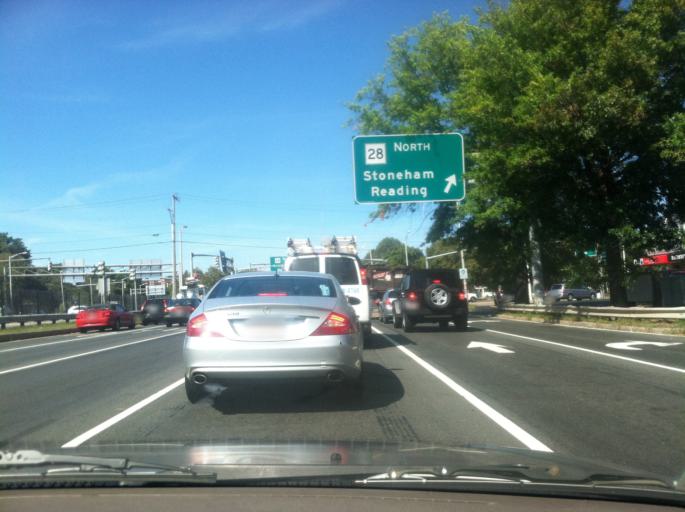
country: US
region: Massachusetts
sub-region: Suffolk County
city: Chelsea
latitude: 42.3873
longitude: -71.0360
